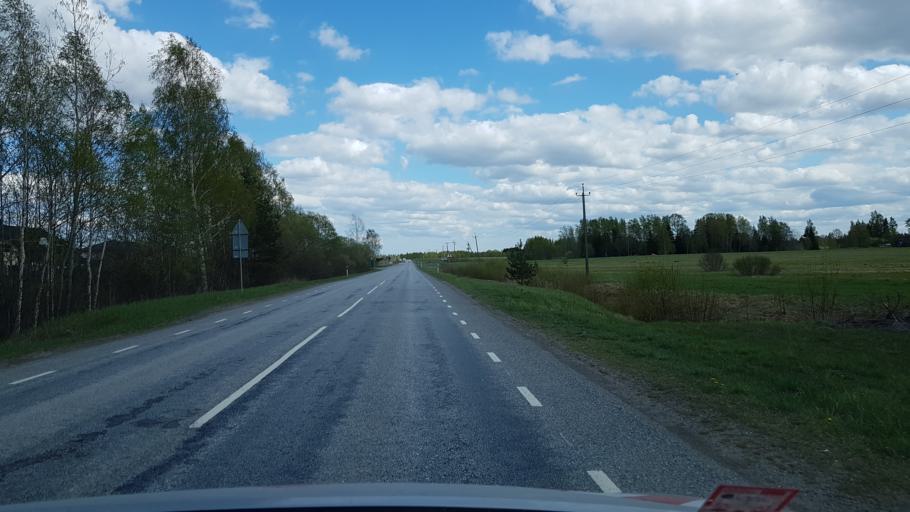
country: EE
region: Tartu
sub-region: UElenurme vald
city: Ulenurme
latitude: 58.3262
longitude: 26.7827
